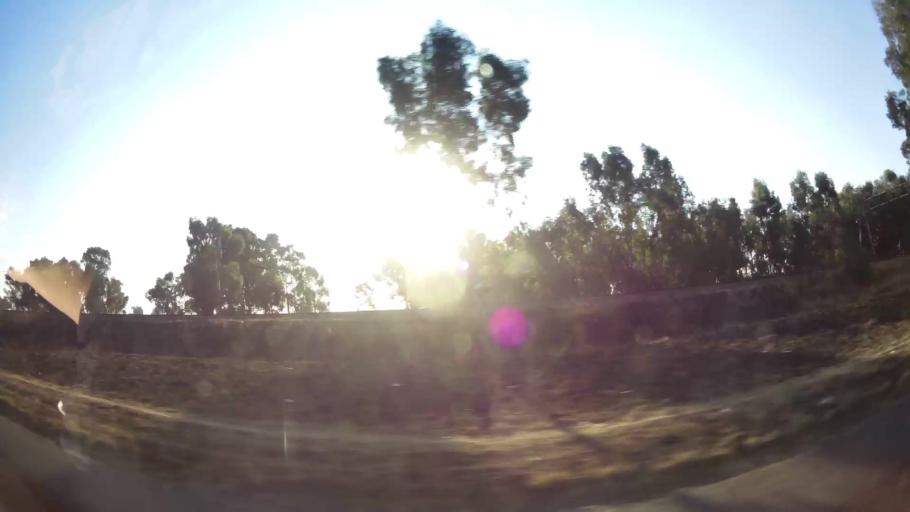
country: ZA
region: Gauteng
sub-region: West Rand District Municipality
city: Randfontein
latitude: -26.1961
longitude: 27.6789
